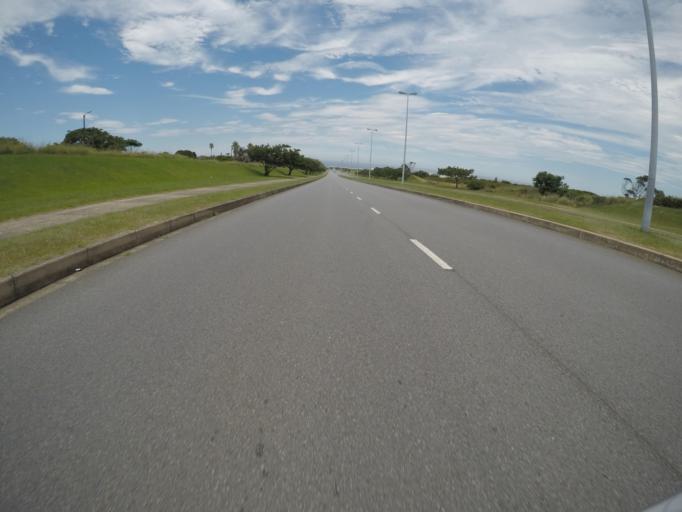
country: ZA
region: Eastern Cape
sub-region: Buffalo City Metropolitan Municipality
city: East London
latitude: -33.0418
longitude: 27.8489
